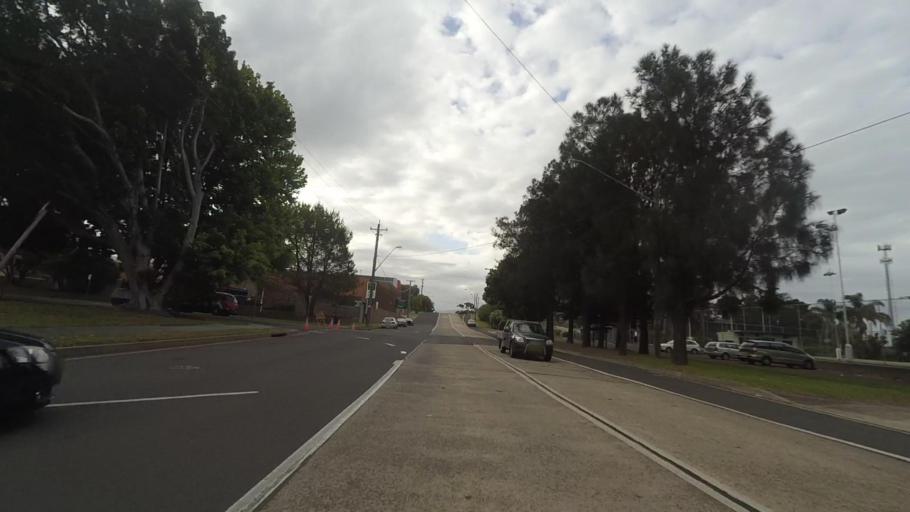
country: AU
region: New South Wales
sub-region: Wollongong
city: Port Kembla
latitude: -34.4808
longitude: 150.9030
